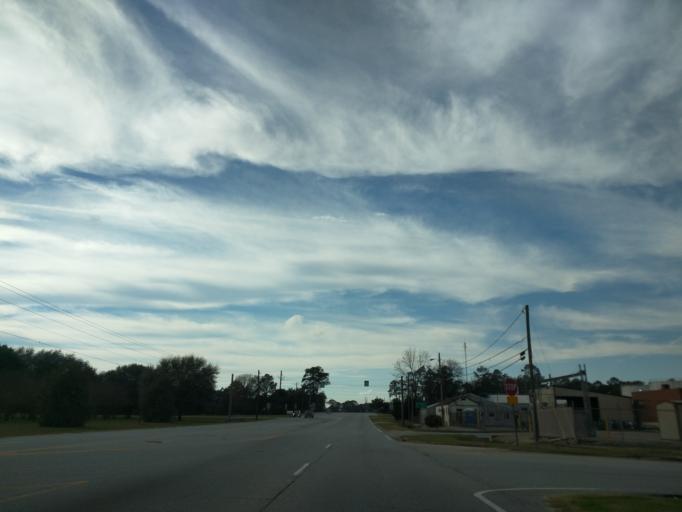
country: US
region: Georgia
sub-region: Decatur County
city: Bainbridge
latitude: 30.9035
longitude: -84.5416
